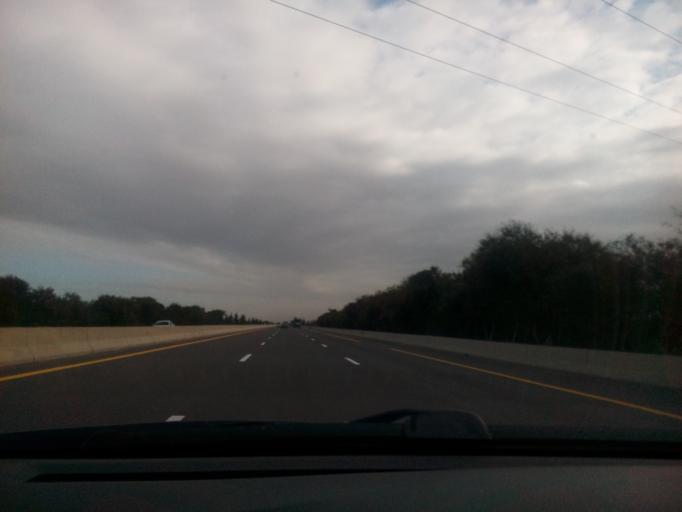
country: DZ
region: Relizane
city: Djidiouia
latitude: 35.9305
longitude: 0.8032
